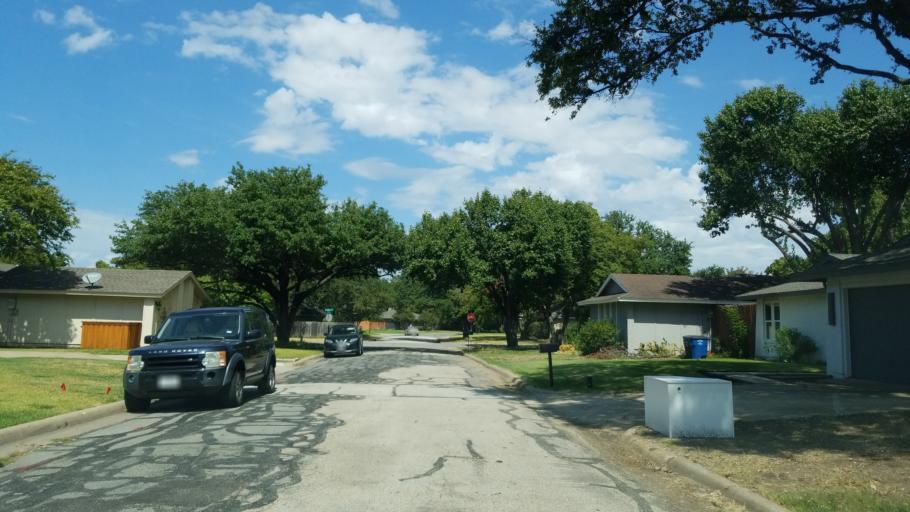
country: US
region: Texas
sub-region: Dallas County
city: Addison
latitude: 32.9640
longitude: -96.7843
